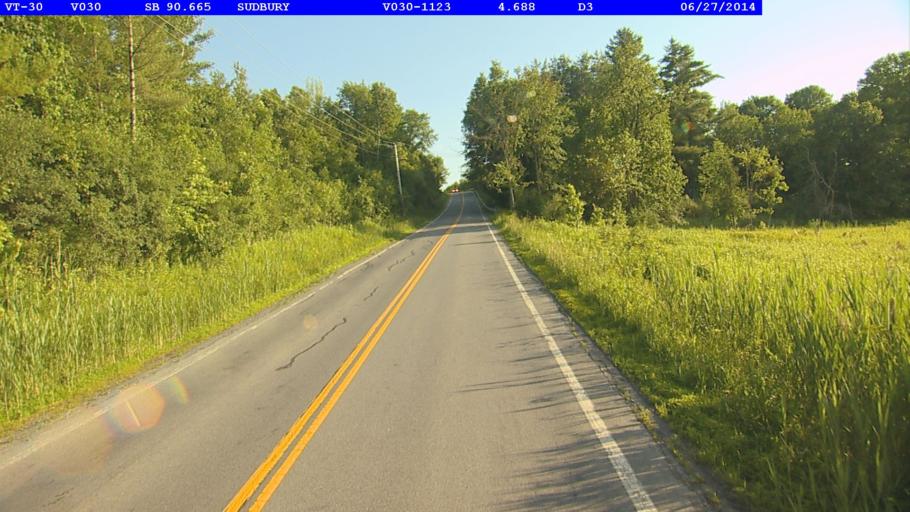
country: US
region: Vermont
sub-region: Rutland County
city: Brandon
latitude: 43.8143
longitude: -73.1972
